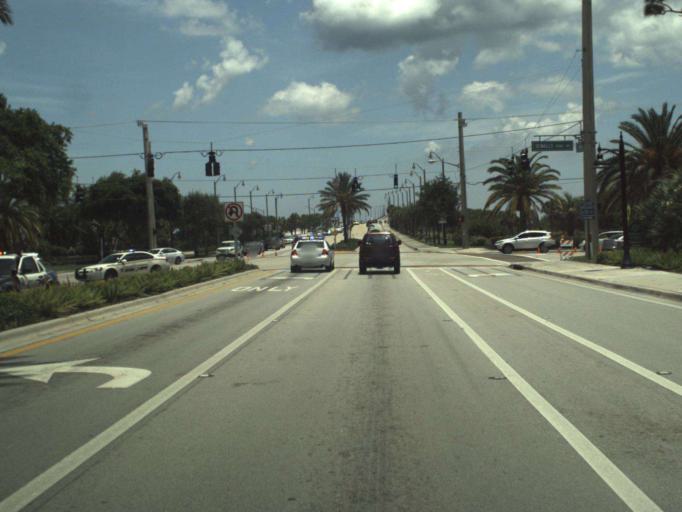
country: US
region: Florida
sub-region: Martin County
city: Sewall's Point
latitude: 27.2026
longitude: -80.2012
